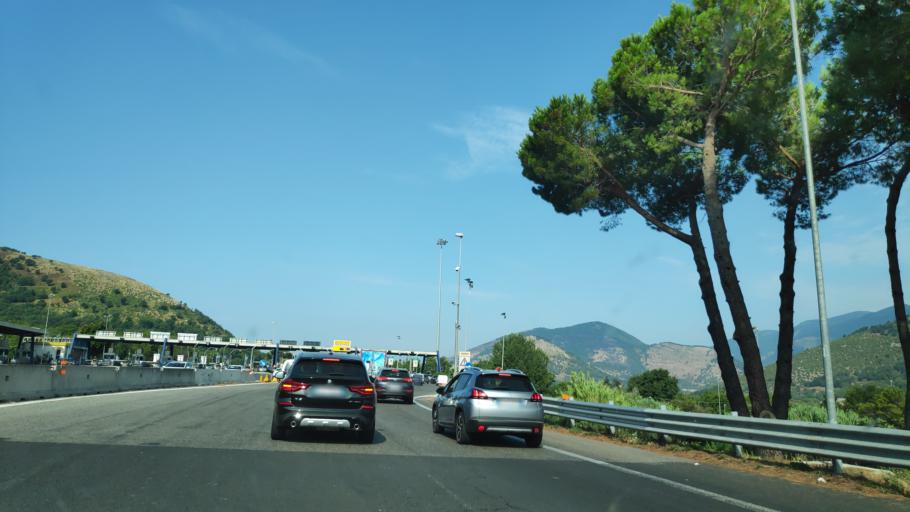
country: IT
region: Campania
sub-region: Provincia di Salerno
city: Piazza del Galdo-Sant'Angelo
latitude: 40.7727
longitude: 14.7288
